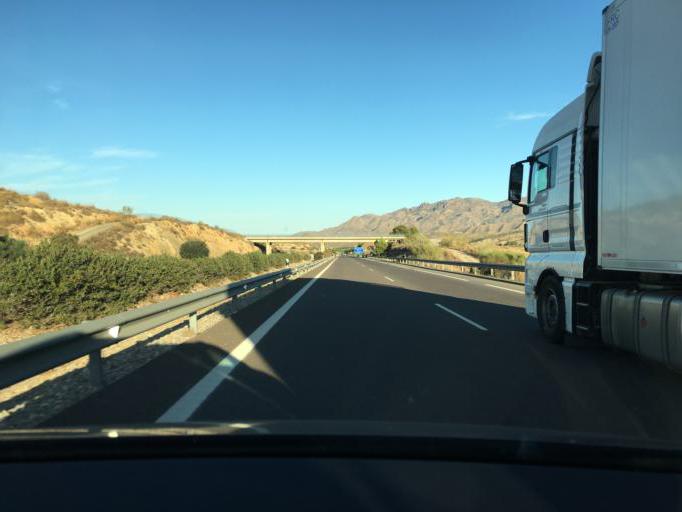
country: ES
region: Andalusia
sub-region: Provincia de Almeria
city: Bedar
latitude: 37.1468
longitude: -1.9766
